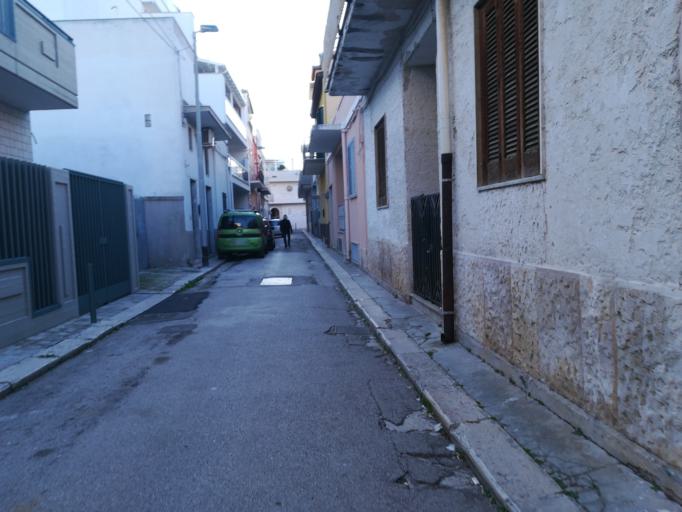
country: IT
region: Apulia
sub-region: Provincia di Bari
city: Modugno
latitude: 41.0795
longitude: 16.7837
